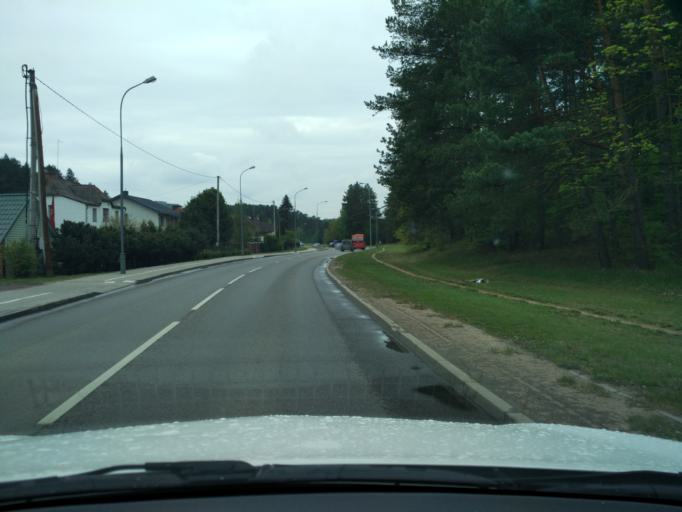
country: LT
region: Vilnius County
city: Rasos
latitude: 54.7271
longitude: 25.3455
